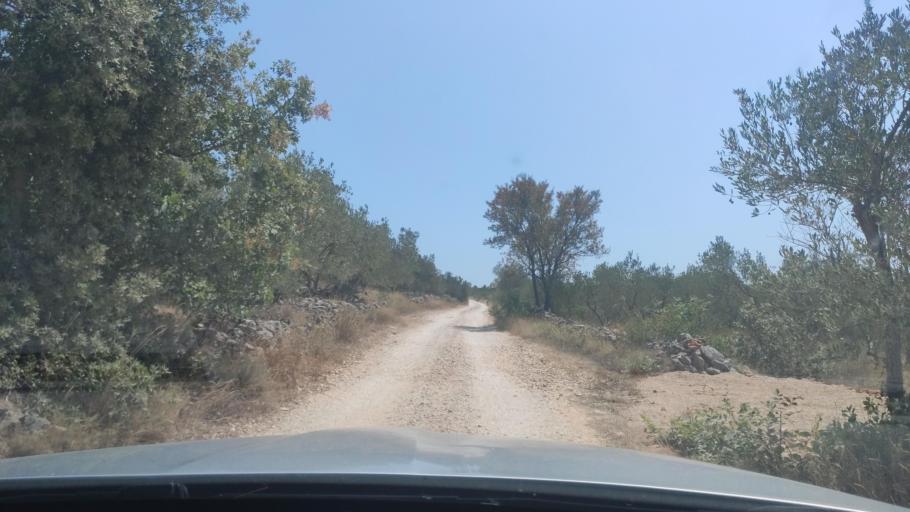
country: HR
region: Sibensko-Kniniska
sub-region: Grad Sibenik
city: Tisno
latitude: 43.7777
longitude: 15.6464
